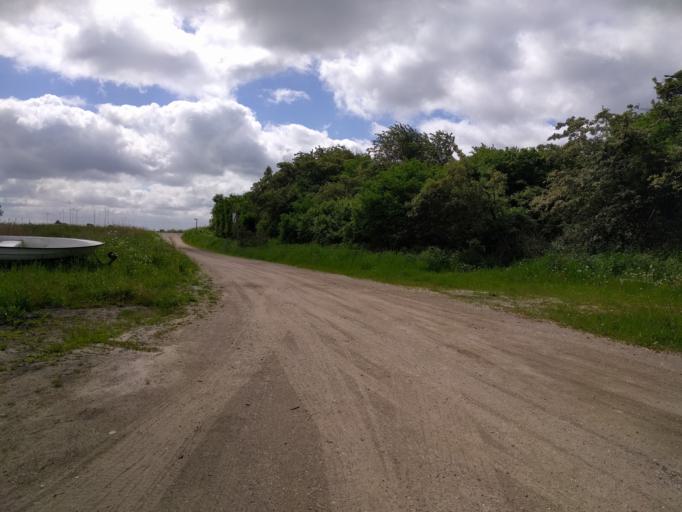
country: DK
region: South Denmark
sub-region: Kerteminde Kommune
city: Kerteminde
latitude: 55.4386
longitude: 10.6386
